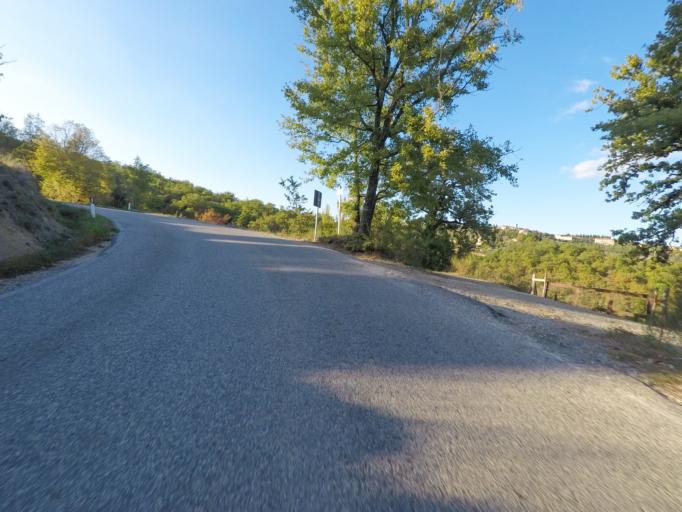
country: IT
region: Tuscany
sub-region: Provincia di Siena
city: Radda in Chianti
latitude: 43.4764
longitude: 11.3737
